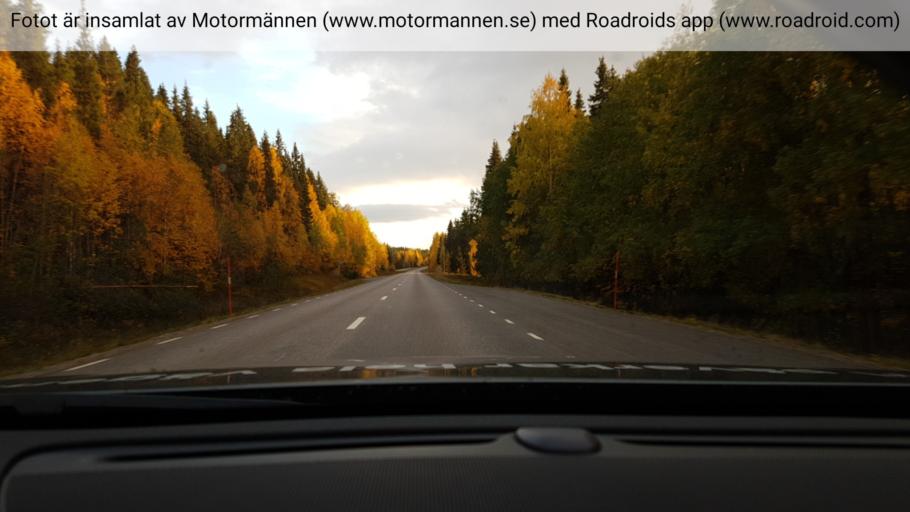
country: SE
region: Norrbotten
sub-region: Overkalix Kommun
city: OEverkalix
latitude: 66.5582
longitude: 22.7603
